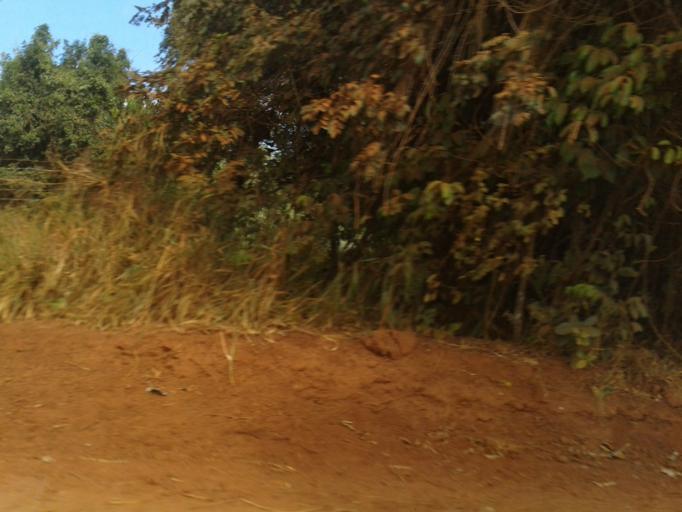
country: BR
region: Minas Gerais
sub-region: Ituiutaba
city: Ituiutaba
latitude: -19.0411
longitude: -49.3782
